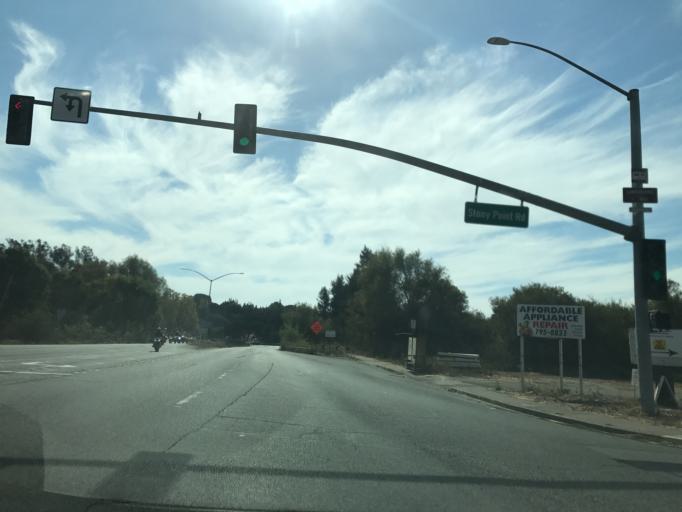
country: US
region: California
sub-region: Sonoma County
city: Penngrove
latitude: 38.2691
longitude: -122.6708
